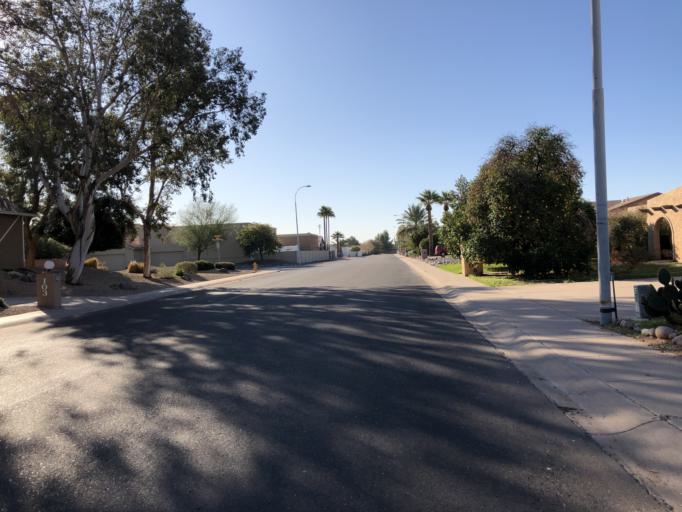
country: US
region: Arizona
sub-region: Maricopa County
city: Chandler
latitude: 33.3015
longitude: -111.9188
